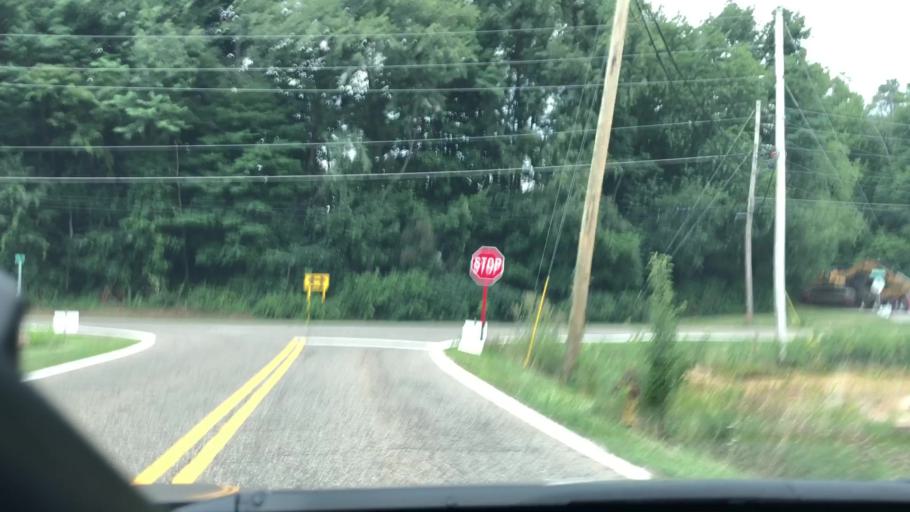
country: US
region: Ohio
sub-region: Summit County
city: New Franklin
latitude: 40.9093
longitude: -81.5170
